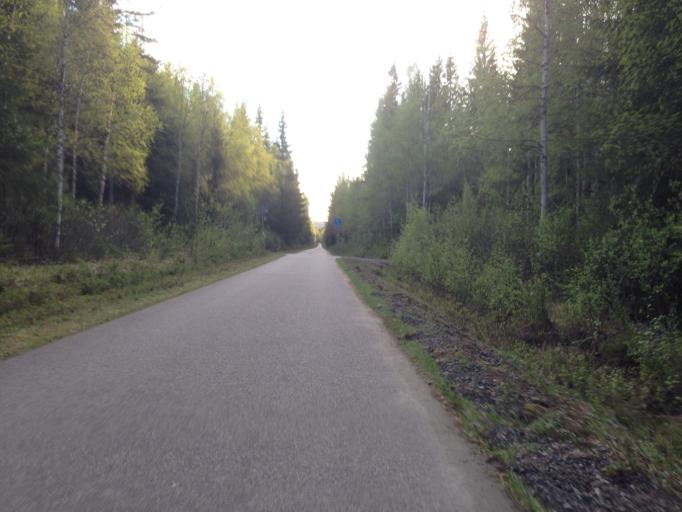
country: SE
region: Dalarna
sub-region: Ludvika Kommun
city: Ludvika
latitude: 60.1401
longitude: 15.1166
